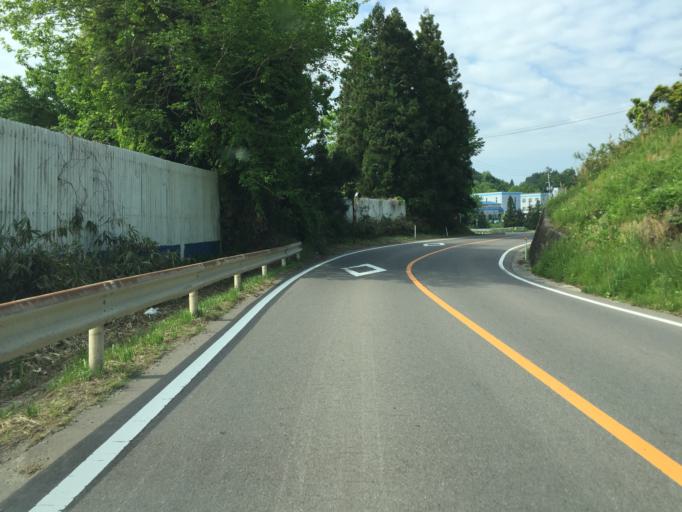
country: JP
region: Fukushima
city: Fukushima-shi
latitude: 37.6610
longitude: 140.5120
